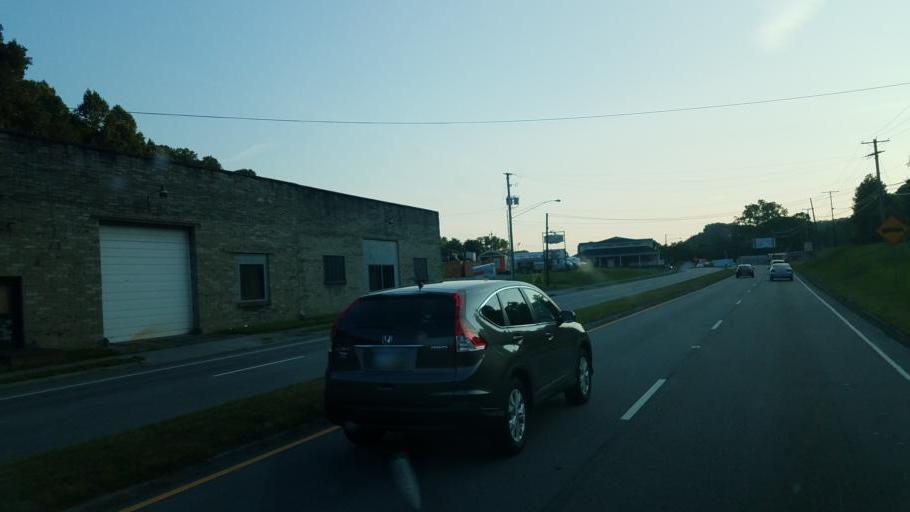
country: US
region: Virginia
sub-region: Scott County
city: Weber City
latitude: 36.6227
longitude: -82.5627
